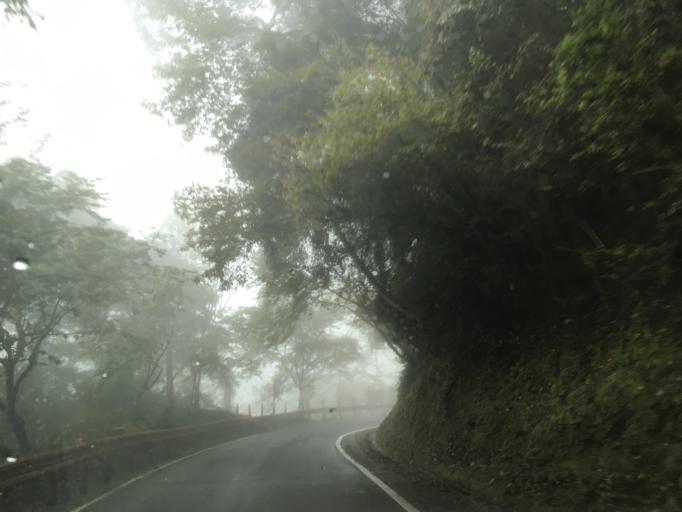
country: TW
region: Taiwan
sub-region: Hualien
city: Hualian
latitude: 24.1911
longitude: 121.4198
